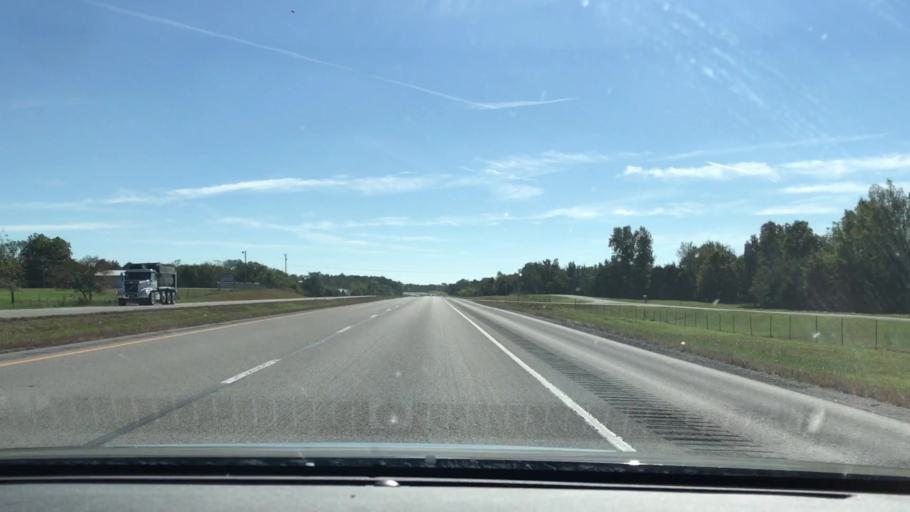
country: US
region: Kentucky
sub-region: Todd County
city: Elkton
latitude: 36.8345
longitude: -87.2344
